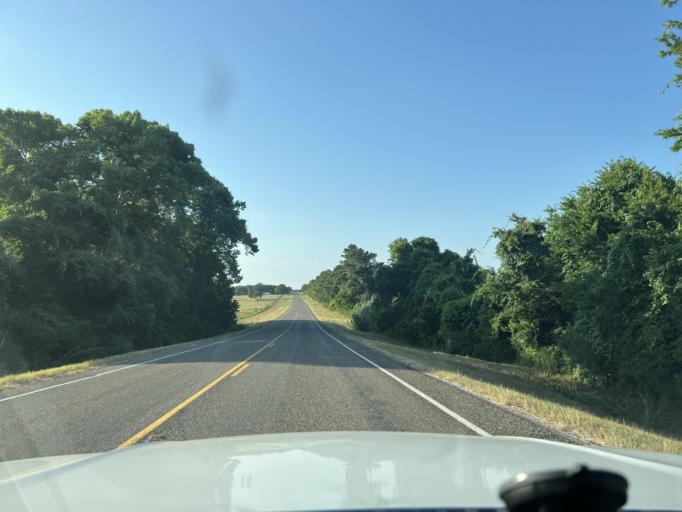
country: US
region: Texas
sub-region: Washington County
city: Brenham
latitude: 30.1847
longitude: -96.3942
